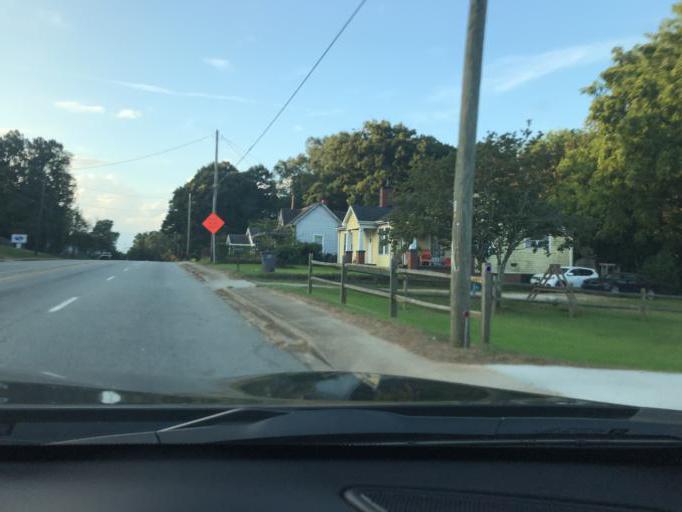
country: US
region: South Carolina
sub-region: Greenville County
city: Welcome
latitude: 34.8328
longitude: -82.4398
